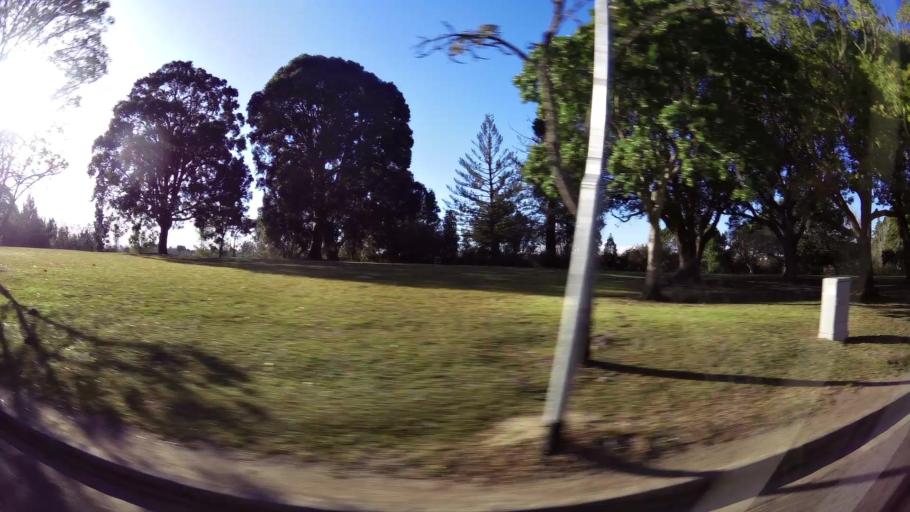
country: ZA
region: Western Cape
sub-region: Eden District Municipality
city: George
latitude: -33.9510
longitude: 22.4544
